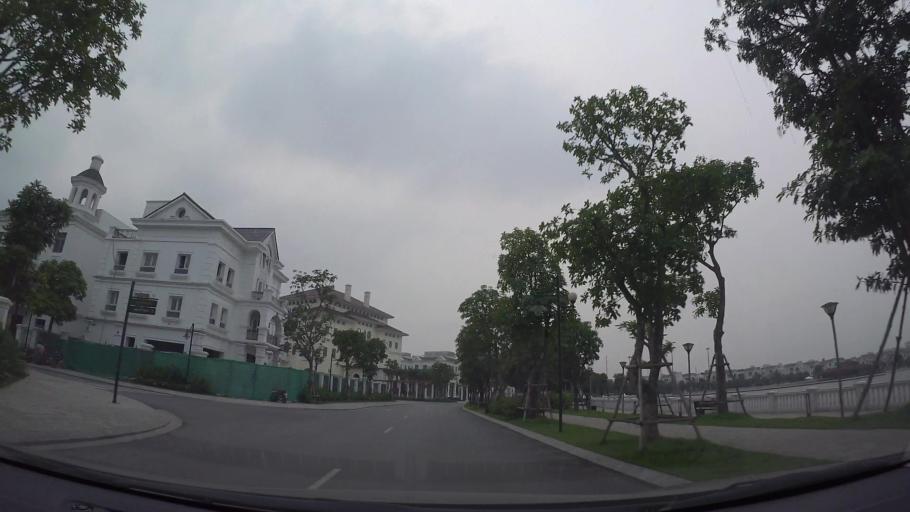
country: VN
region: Ha Noi
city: Trau Quy
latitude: 21.0461
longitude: 105.9062
